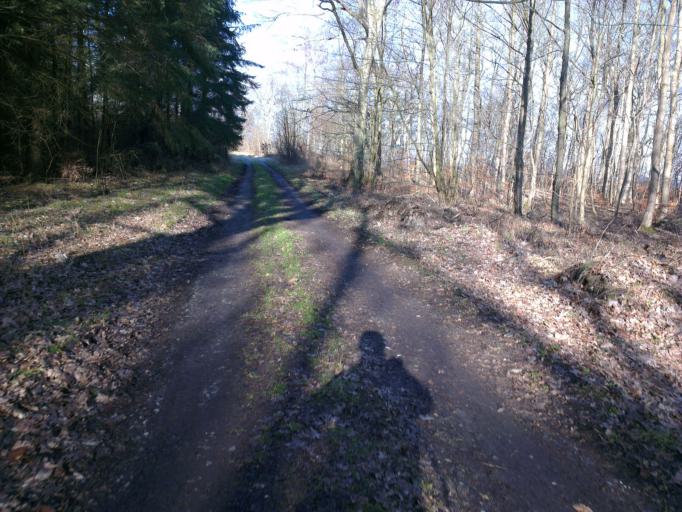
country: DK
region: Capital Region
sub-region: Halsnaes Kommune
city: Frederiksvaerk
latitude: 55.9115
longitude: 12.0049
